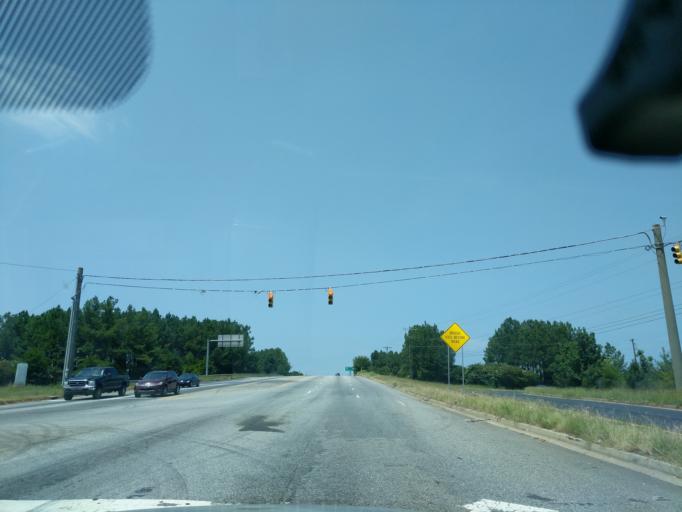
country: US
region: South Carolina
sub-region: Spartanburg County
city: Duncan
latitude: 34.8910
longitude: -82.1583
